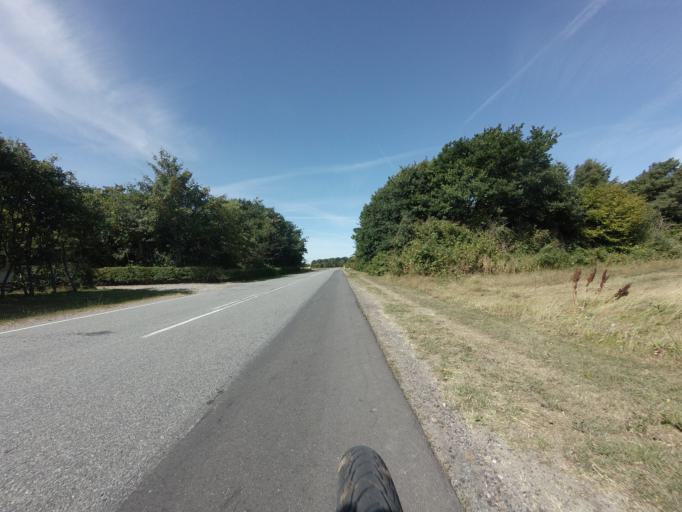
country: DK
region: North Denmark
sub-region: Hjorring Kommune
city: Vra
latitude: 57.3309
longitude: 9.8213
